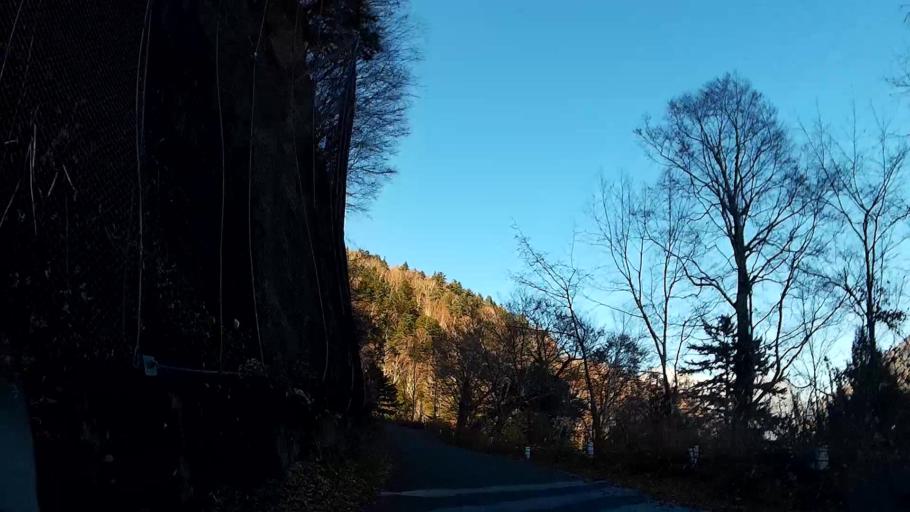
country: JP
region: Nagano
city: Hotaka
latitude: 36.2051
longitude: 137.5977
